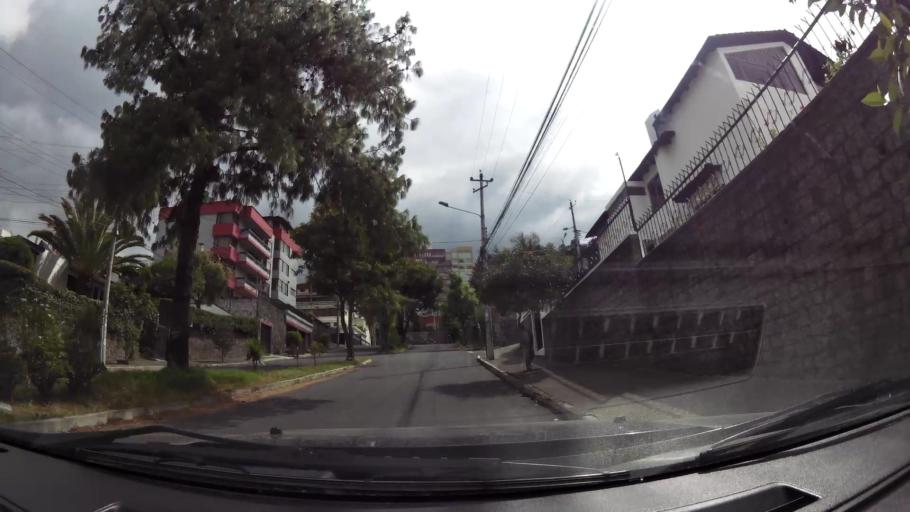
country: EC
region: Pichincha
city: Quito
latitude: -0.1586
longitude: -78.4950
